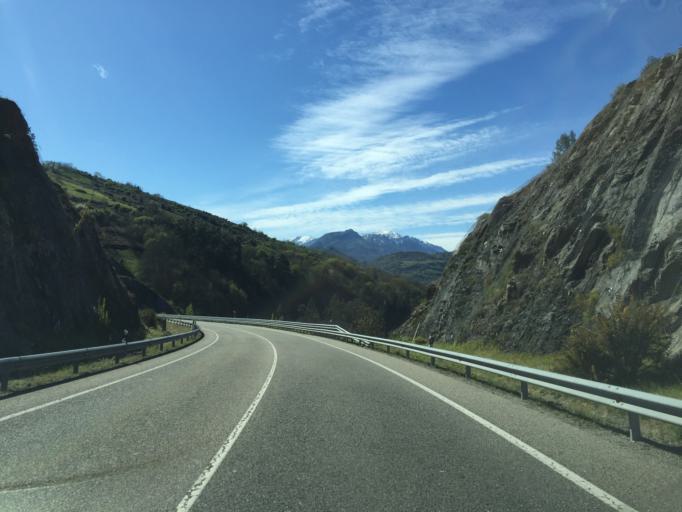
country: ES
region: Asturias
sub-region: Province of Asturias
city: Llanera
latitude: 43.3632
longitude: -5.9598
